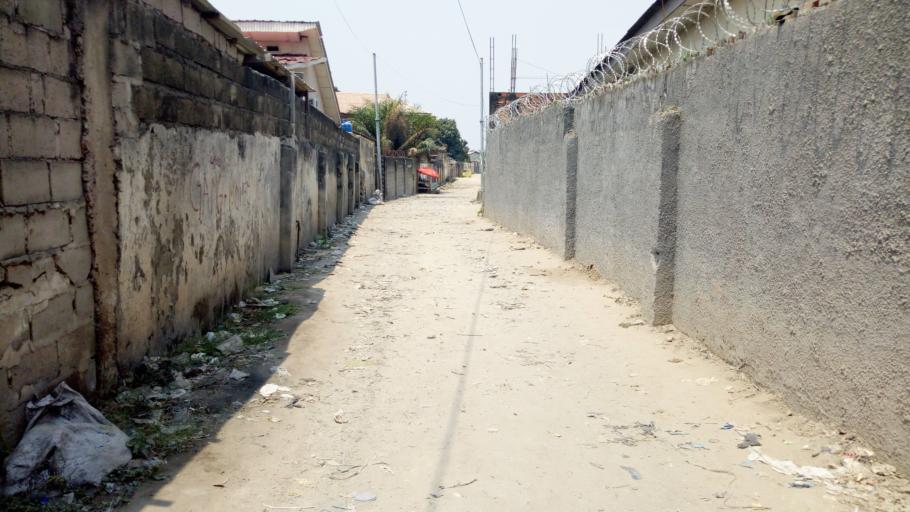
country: CD
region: Kinshasa
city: Kinshasa
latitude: -4.3165
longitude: 15.2932
